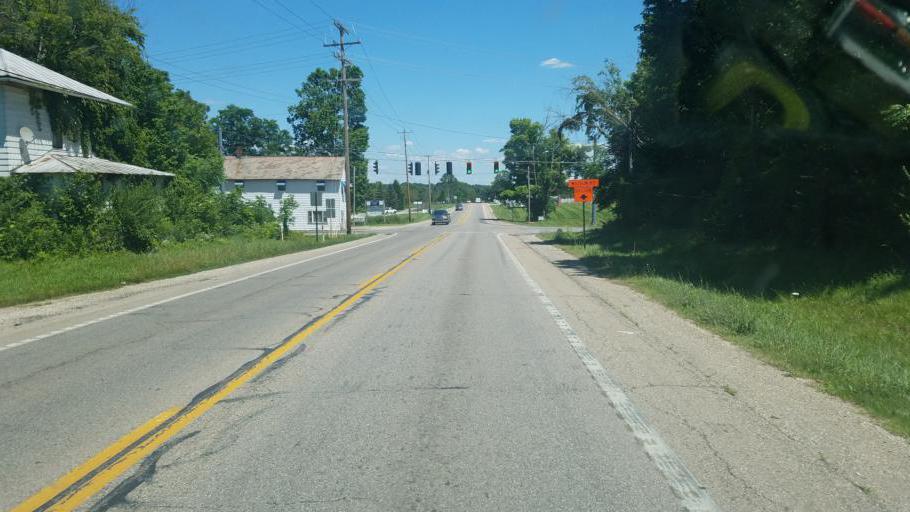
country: US
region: Ohio
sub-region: Delaware County
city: Sunbury
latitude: 40.2655
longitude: -82.9099
